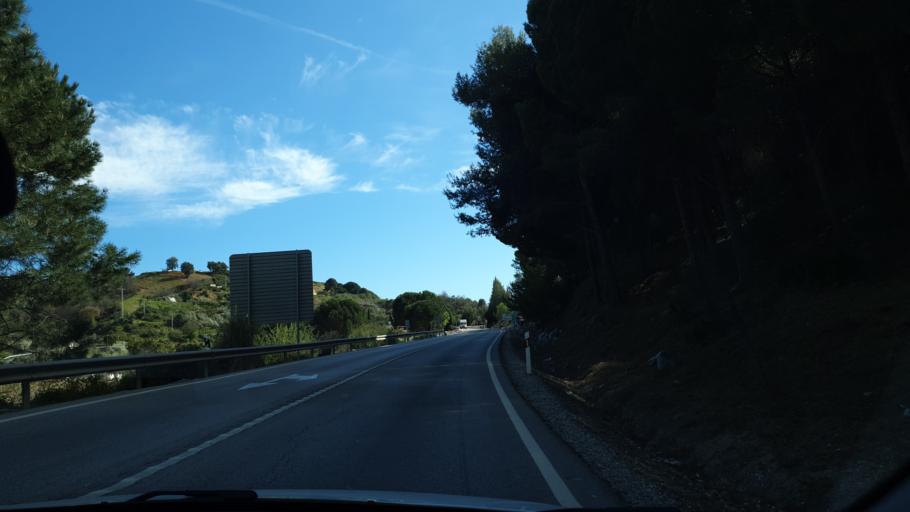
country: ES
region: Andalusia
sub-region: Provincia de Malaga
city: Ojen
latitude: 36.5905
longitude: -4.8519
